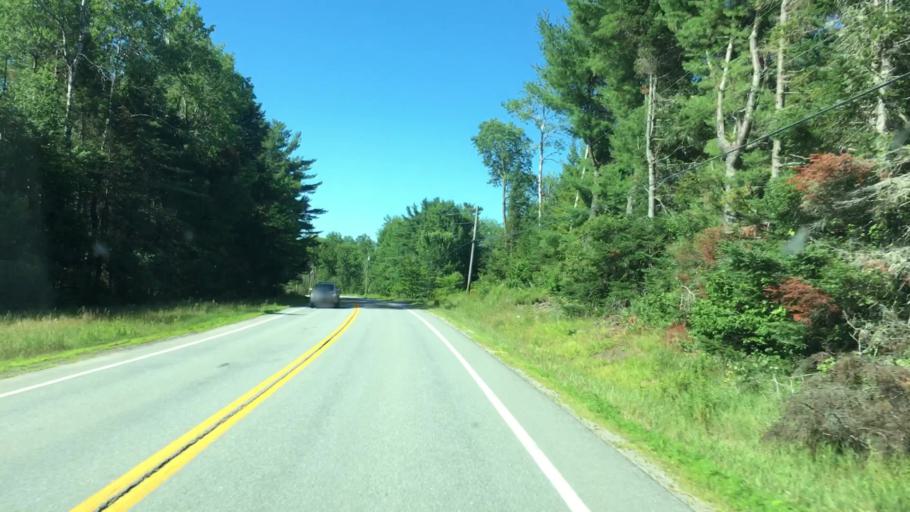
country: US
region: Maine
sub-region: Hancock County
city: Dedham
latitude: 44.6854
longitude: -68.6646
